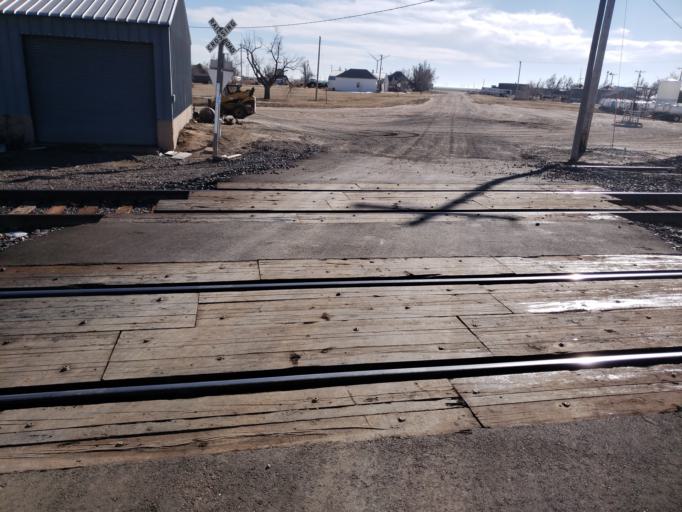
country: US
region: Kansas
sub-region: Ford County
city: Dodge City
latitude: 37.4881
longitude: -99.8974
